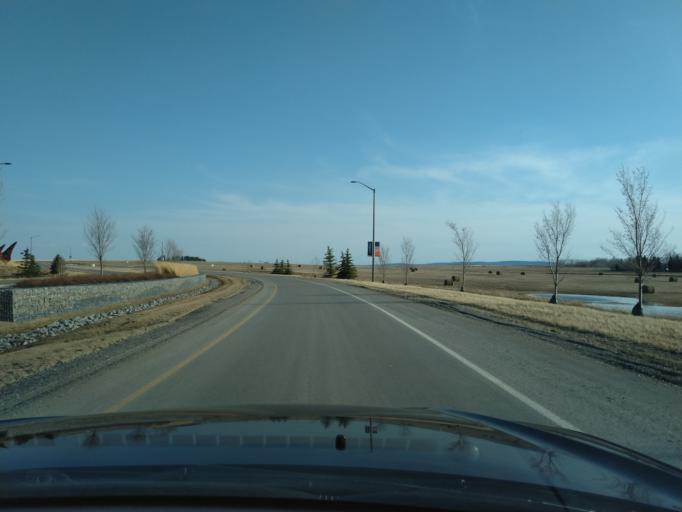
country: CA
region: Alberta
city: Cochrane
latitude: 51.1065
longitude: -114.3924
